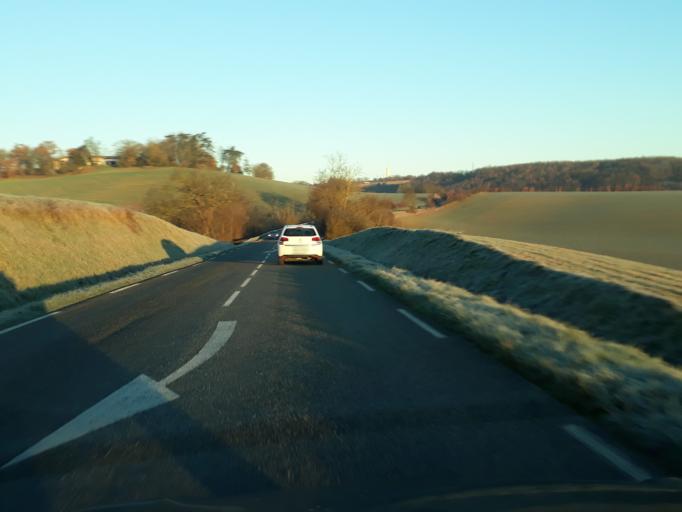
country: FR
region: Midi-Pyrenees
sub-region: Departement du Gers
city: Pavie
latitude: 43.6259
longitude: 0.6364
